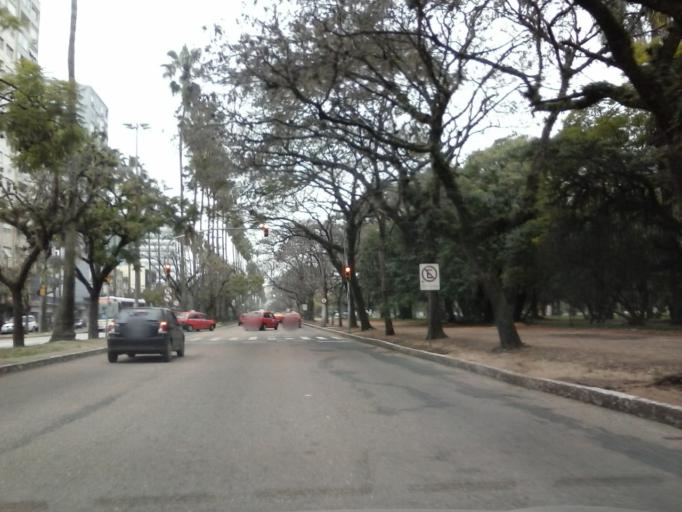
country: BR
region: Rio Grande do Sul
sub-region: Porto Alegre
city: Porto Alegre
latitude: -30.0338
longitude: -51.2151
